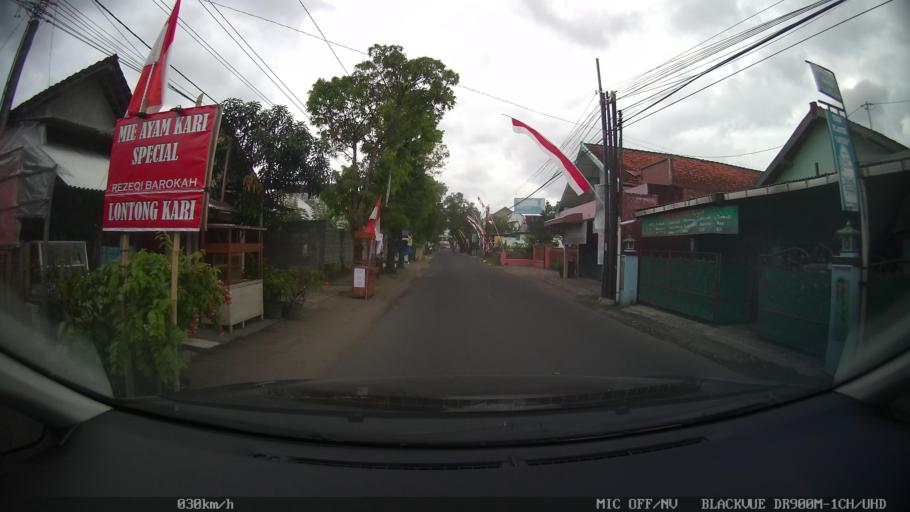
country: ID
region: Daerah Istimewa Yogyakarta
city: Sewon
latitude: -7.8319
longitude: 110.4126
